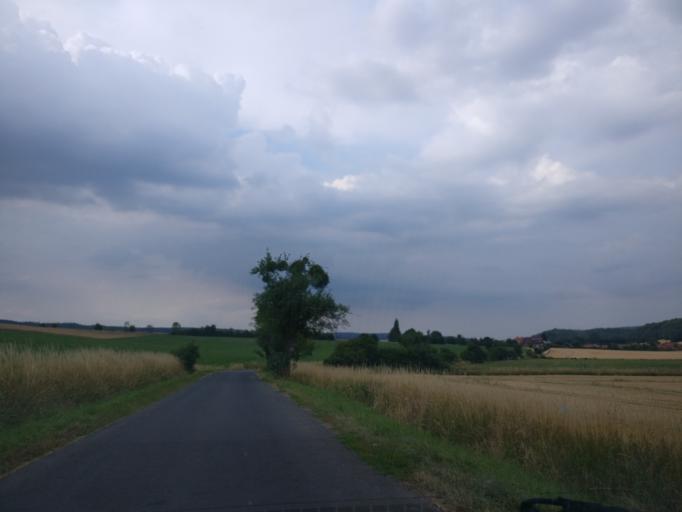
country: DE
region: Lower Saxony
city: Adelebsen
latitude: 51.5883
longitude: 9.7788
